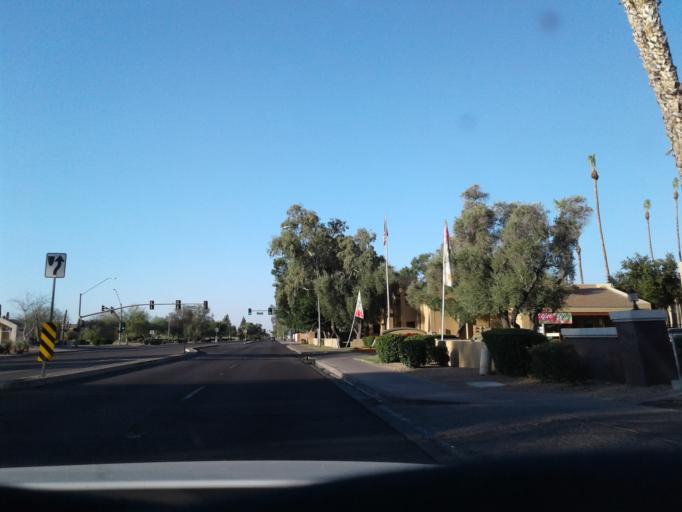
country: US
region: Arizona
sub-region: Maricopa County
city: Peoria
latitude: 33.6216
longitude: -112.1858
